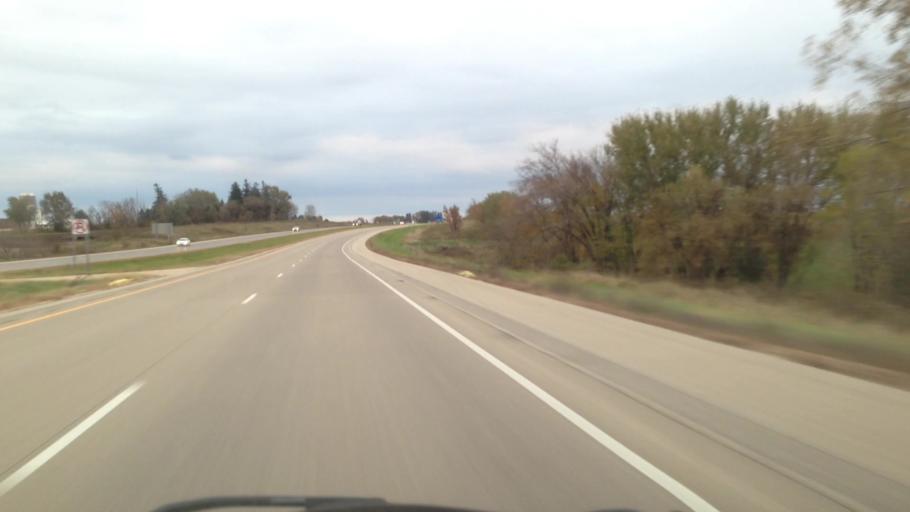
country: US
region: Minnesota
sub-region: Winona County
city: Winona
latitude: 43.9262
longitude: -91.6150
